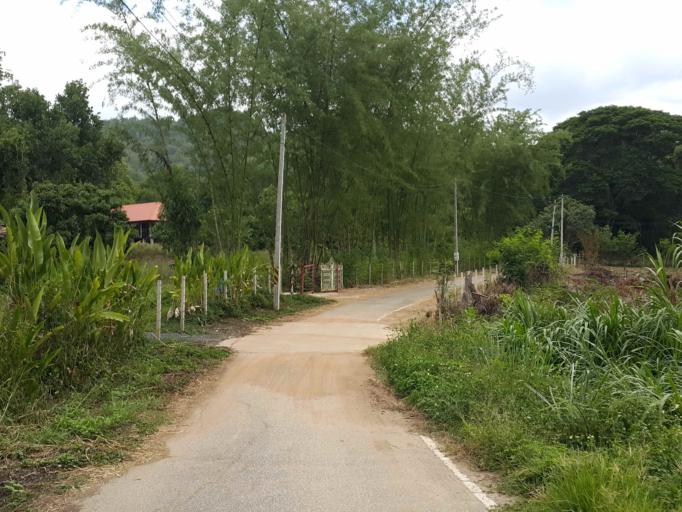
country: TH
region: Chiang Mai
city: Hang Dong
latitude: 18.7556
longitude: 98.9036
